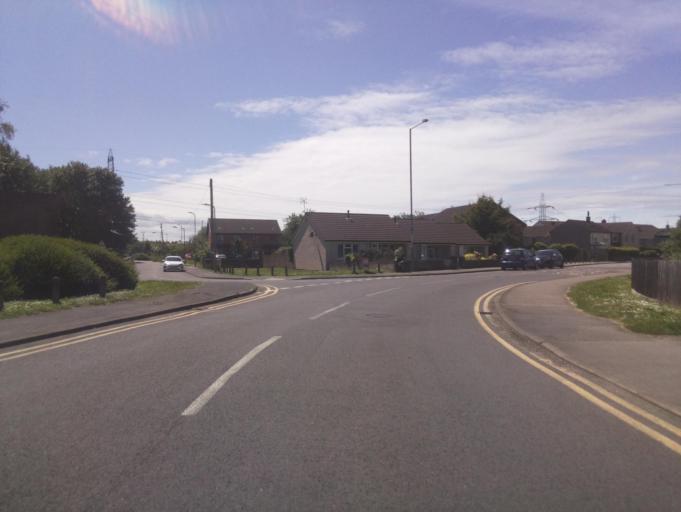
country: GB
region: Wales
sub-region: Monmouthshire
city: Caldicot
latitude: 51.5862
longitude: -2.7589
